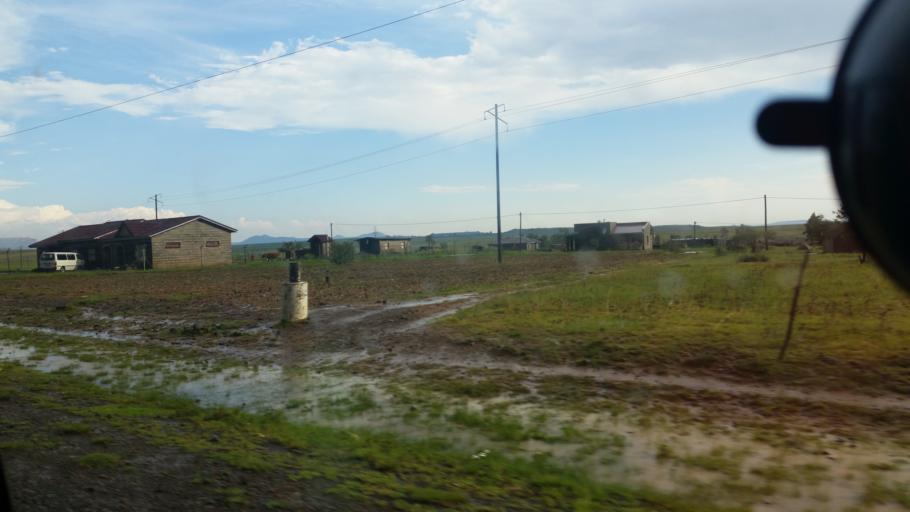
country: LS
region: Mafeteng
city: Mafeteng
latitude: -29.7720
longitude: 27.1875
